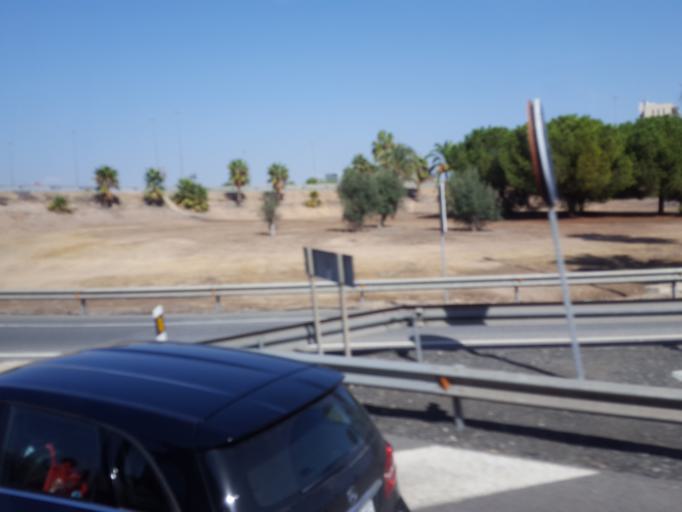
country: ES
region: Murcia
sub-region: Murcia
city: Murcia
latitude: 37.9984
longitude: -1.1520
